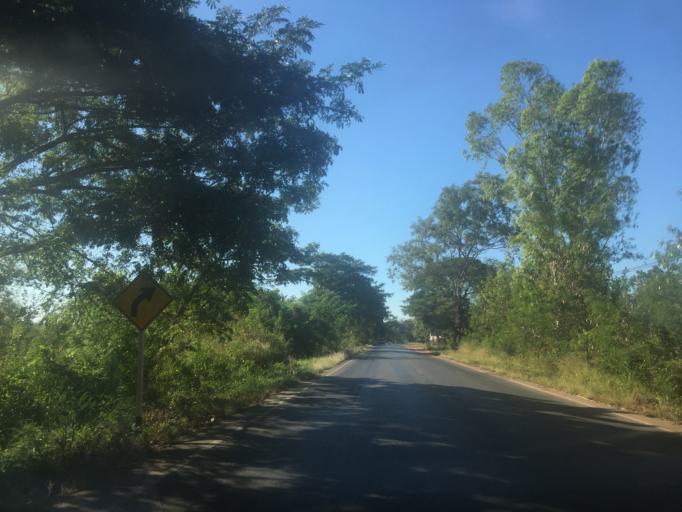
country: TH
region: Kalasin
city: Tha Khantho
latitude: 16.9632
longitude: 103.2509
